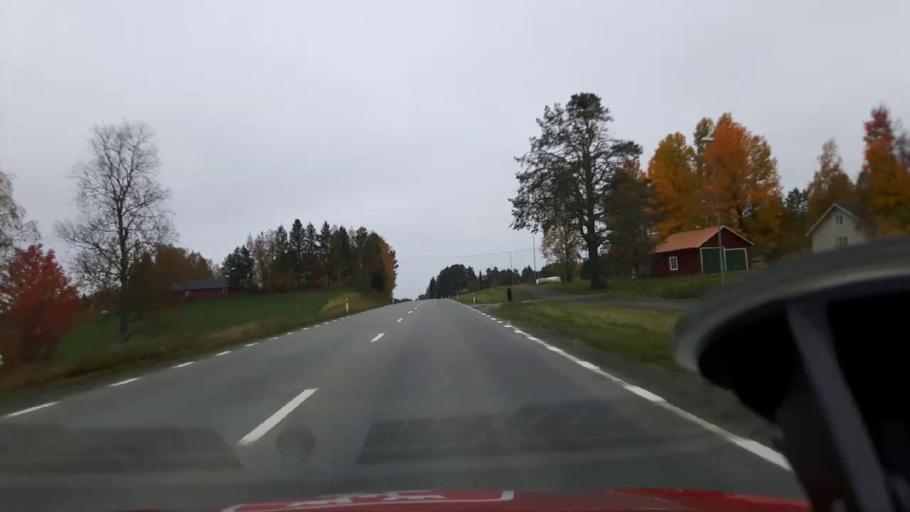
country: SE
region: Jaemtland
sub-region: Bergs Kommun
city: Hoverberg
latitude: 62.7007
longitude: 14.4080
